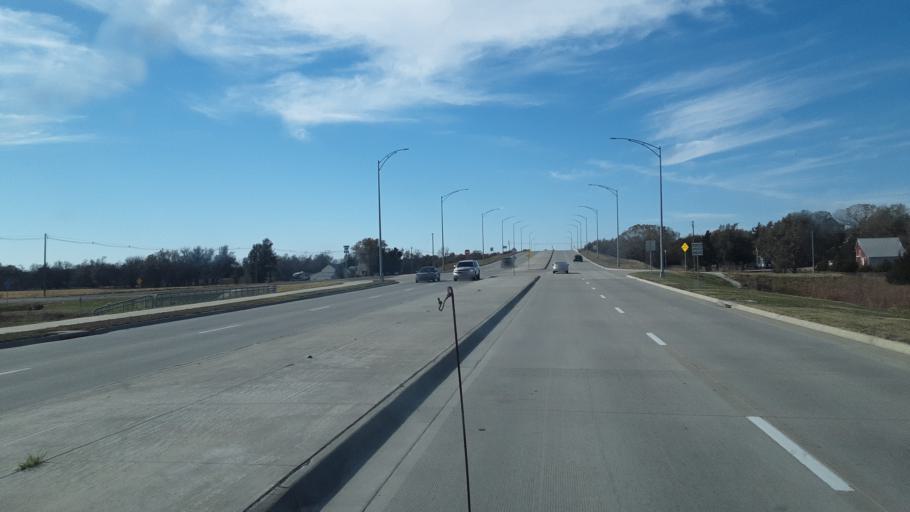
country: US
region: Kansas
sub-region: McPherson County
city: McPherson
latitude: 38.3703
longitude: -97.6340
